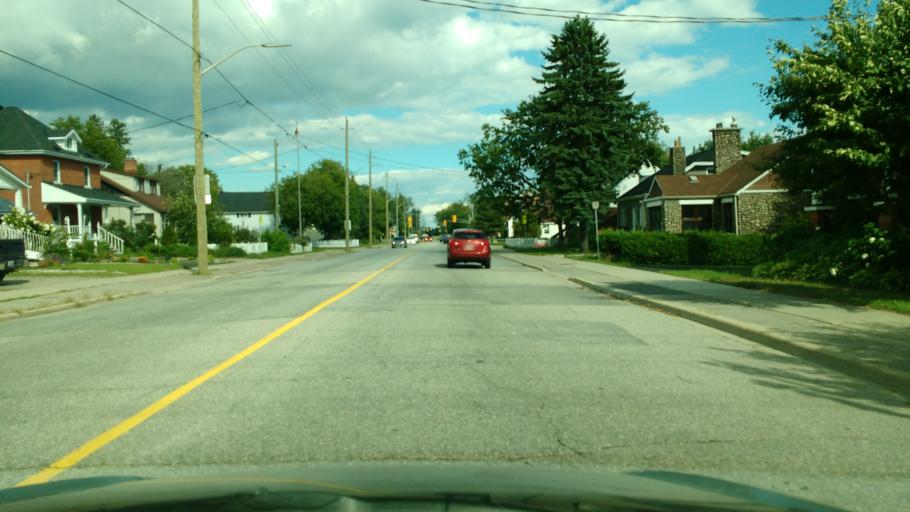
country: CA
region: Ontario
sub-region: Nipissing District
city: North Bay
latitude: 46.3179
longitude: -79.4520
